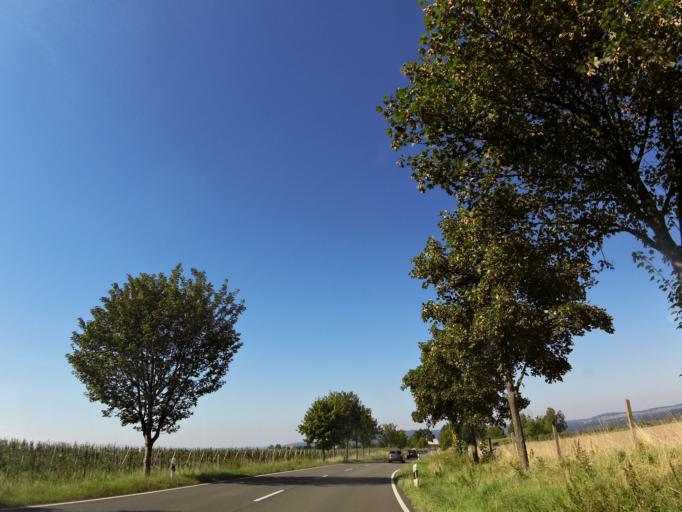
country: DE
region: Saxony
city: Dohma
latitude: 50.9326
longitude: 13.9708
